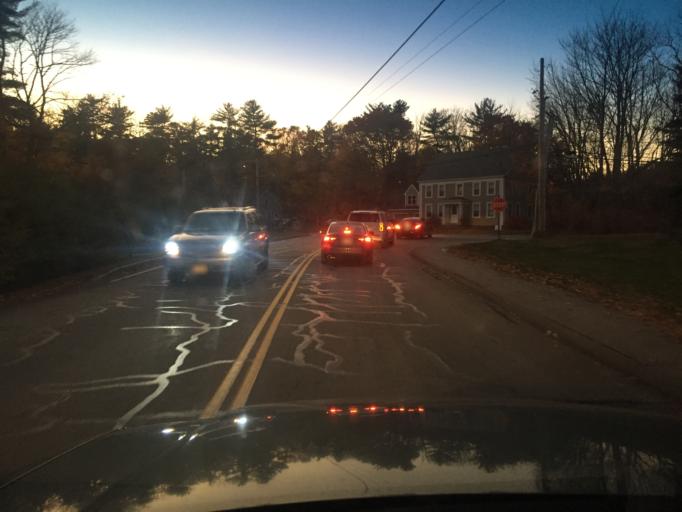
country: US
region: Maine
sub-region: York County
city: York Harbor
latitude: 43.1494
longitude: -70.6398
